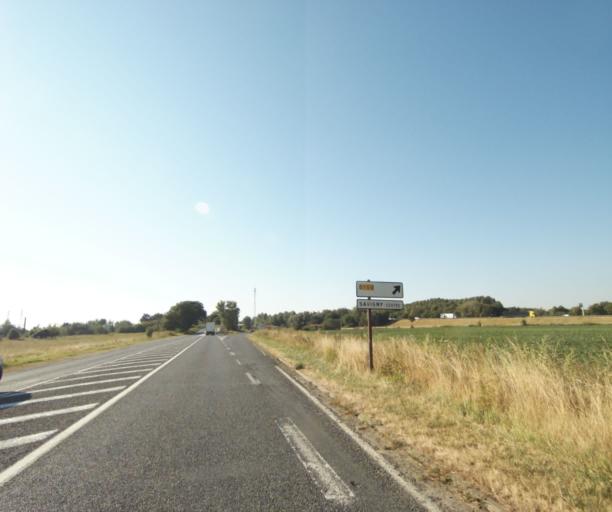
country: FR
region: Ile-de-France
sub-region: Departement de Seine-et-Marne
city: Moissy-Cramayel
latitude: 48.6128
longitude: 2.5741
